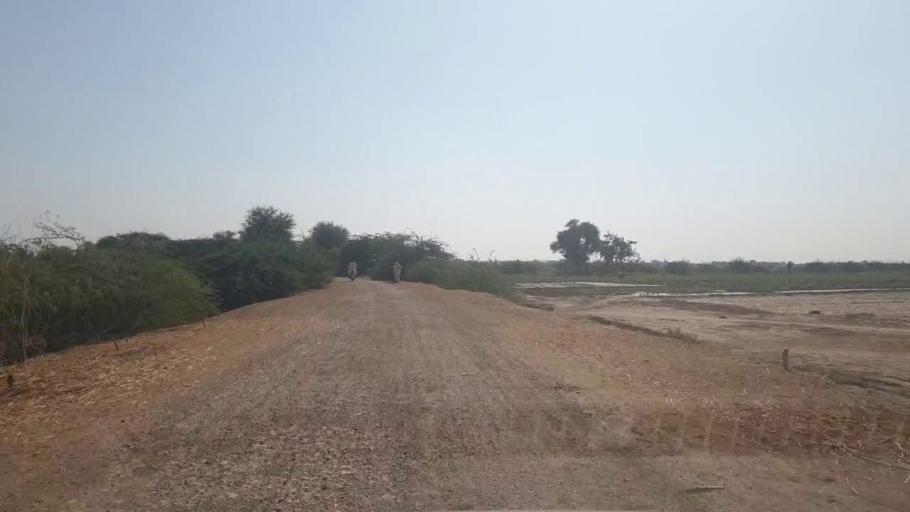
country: PK
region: Sindh
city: Badin
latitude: 24.5566
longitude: 68.8457
